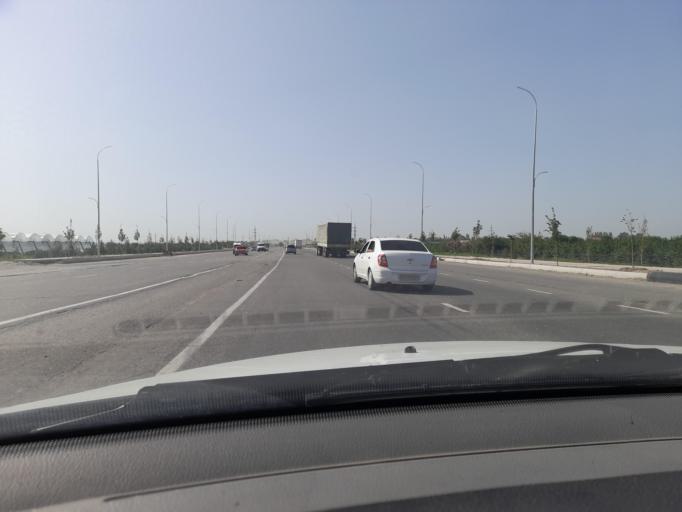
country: UZ
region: Samarqand
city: Daxbet
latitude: 39.7368
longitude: 66.9310
